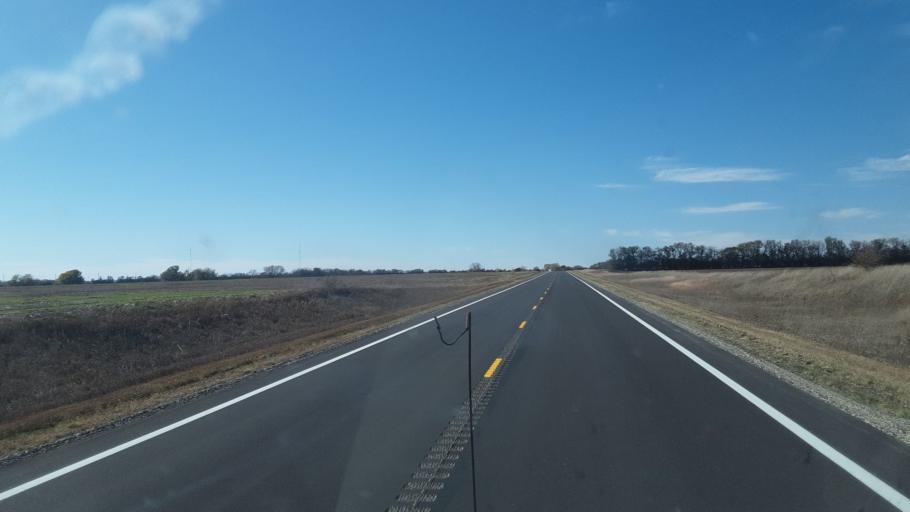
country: US
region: Kansas
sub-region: Rice County
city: Lyons
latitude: 38.3766
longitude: -98.1141
